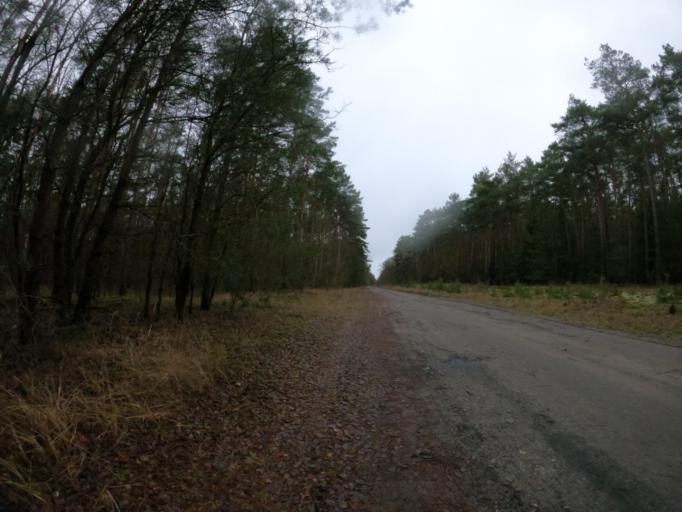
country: PL
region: West Pomeranian Voivodeship
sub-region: Powiat mysliborski
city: Debno
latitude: 52.7961
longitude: 14.7579
